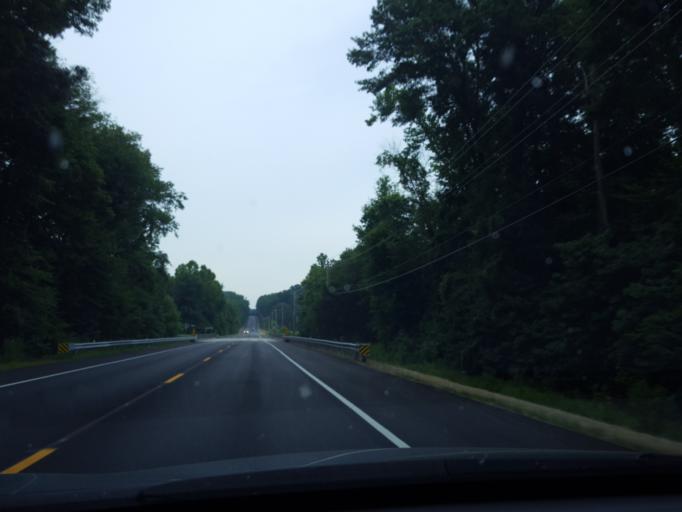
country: US
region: Maryland
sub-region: Charles County
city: La Plata
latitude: 38.4168
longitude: -76.9038
